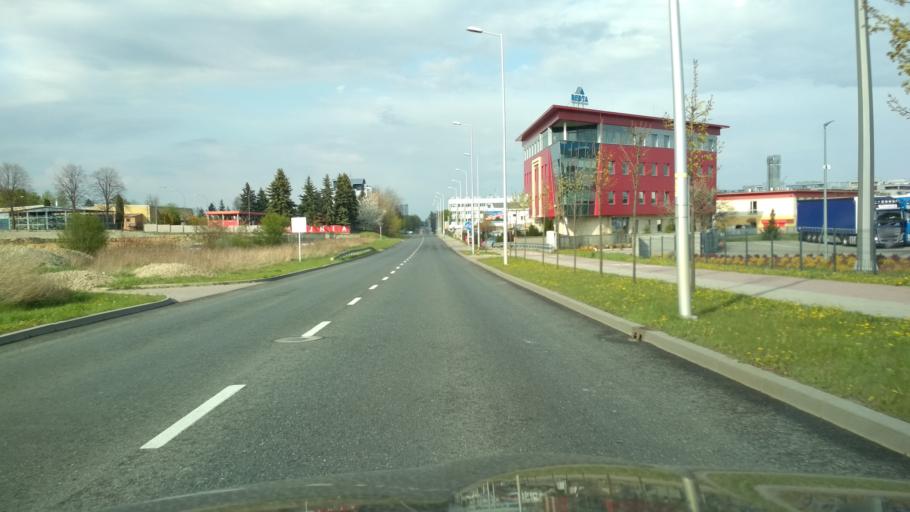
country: PL
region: Subcarpathian Voivodeship
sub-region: Powiat rzeszowski
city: Kielanowka
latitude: 50.0160
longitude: 21.9616
